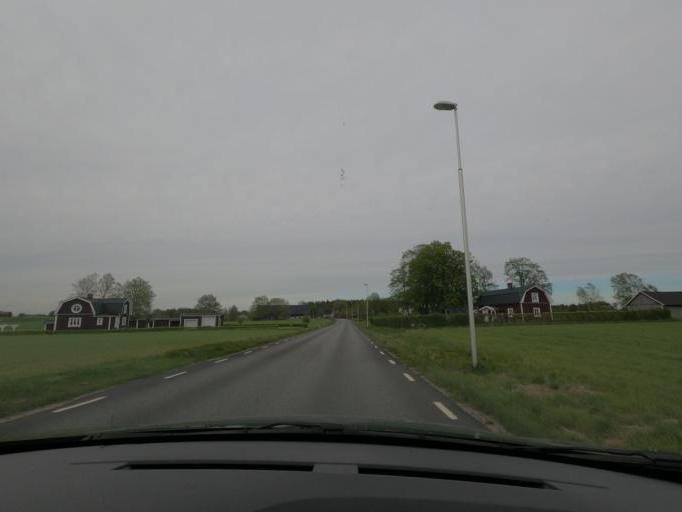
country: SE
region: Joenkoeping
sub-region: Varnamo Kommun
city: Bredaryd
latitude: 57.1328
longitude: 13.7064
